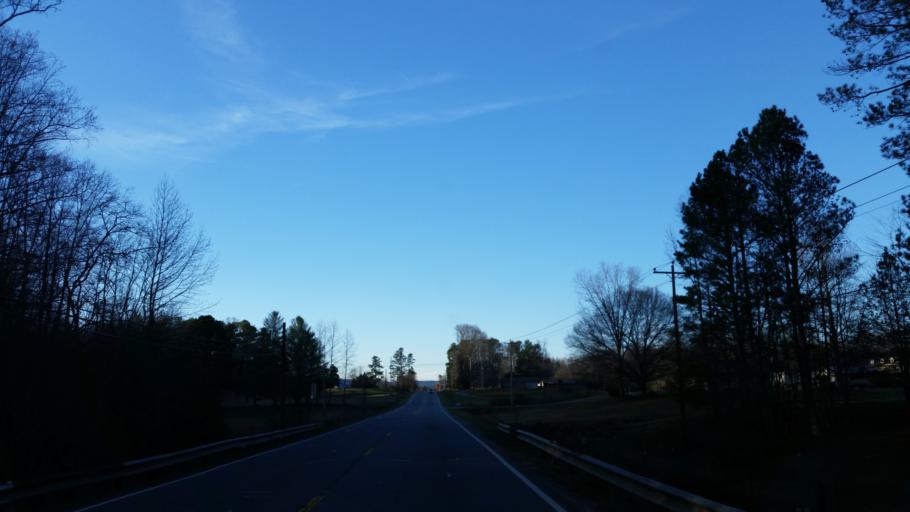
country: US
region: Georgia
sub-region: Whitfield County
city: Dalton
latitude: 34.6382
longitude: -84.9643
